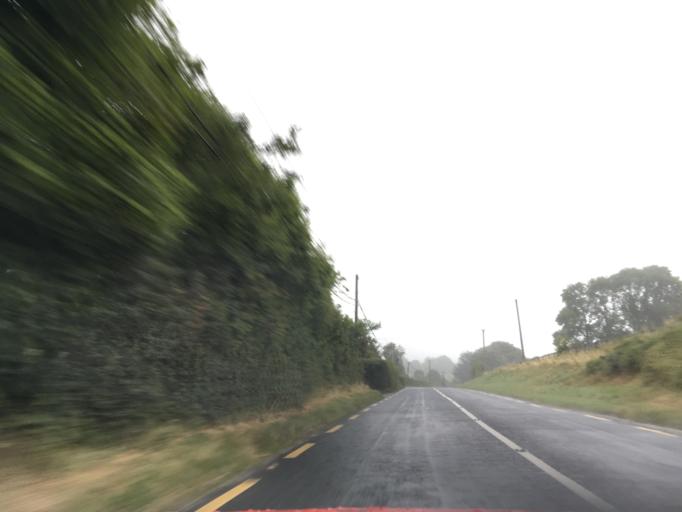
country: IE
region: Munster
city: Tipperary
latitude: 52.4781
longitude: -8.1360
